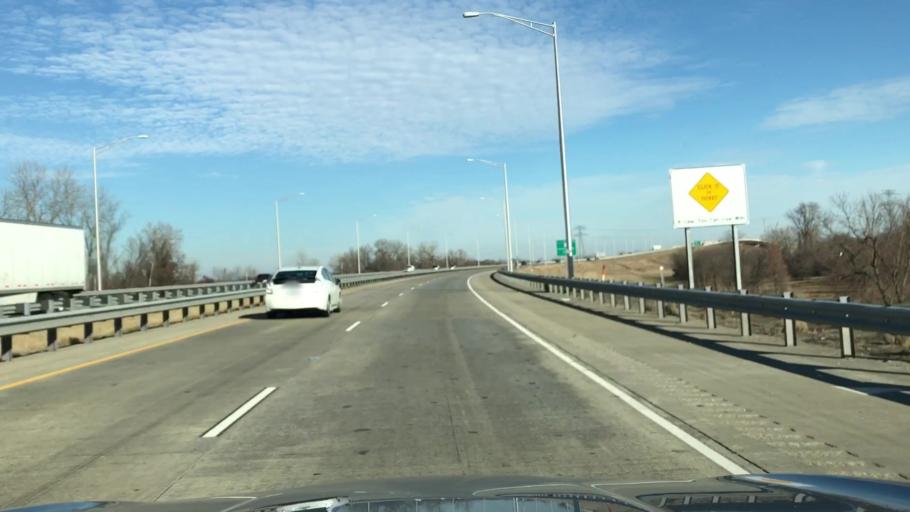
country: US
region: Missouri
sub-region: Saint Louis County
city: Glasgow Village
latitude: 38.7637
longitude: -90.1481
